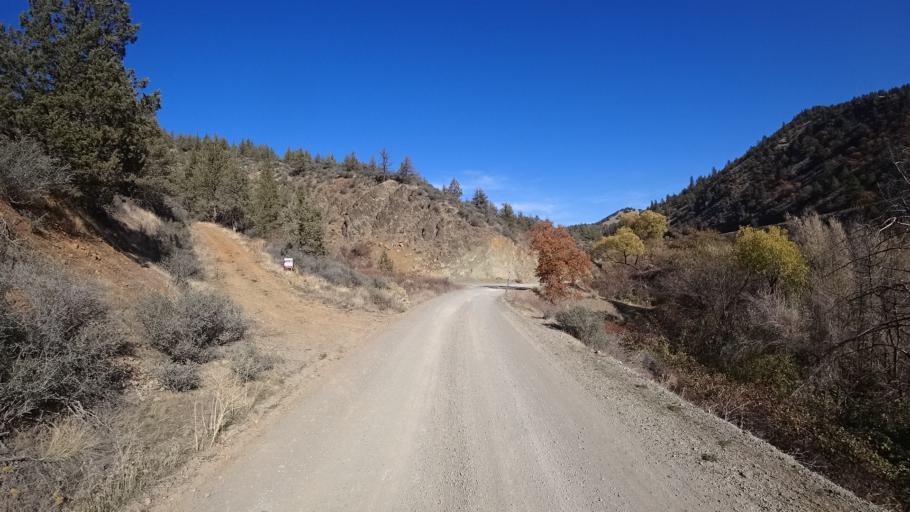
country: US
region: California
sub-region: Siskiyou County
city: Yreka
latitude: 41.7941
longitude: -122.6108
